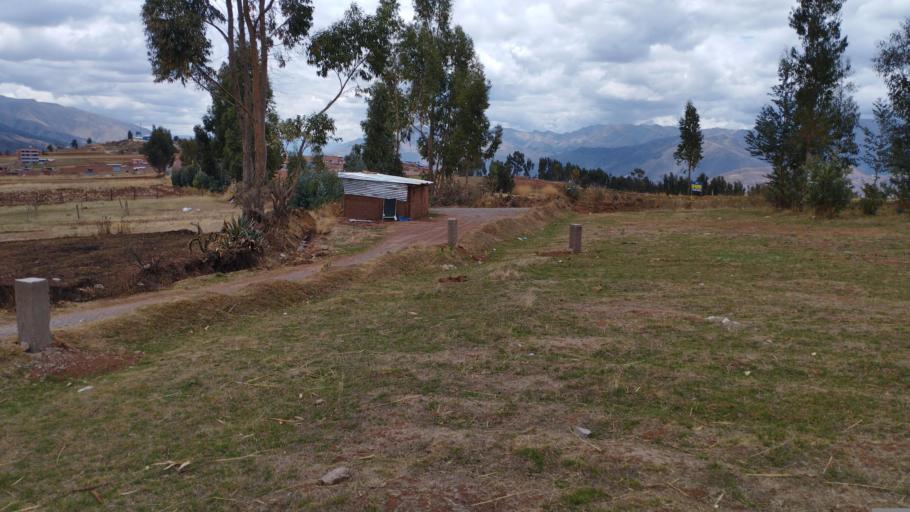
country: PE
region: Cusco
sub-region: Provincia de Cusco
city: Cusco
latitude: -13.5114
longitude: -71.9401
